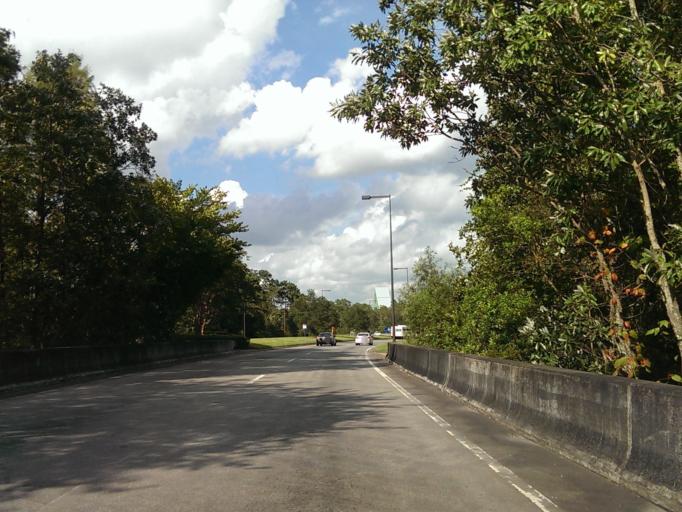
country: US
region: Florida
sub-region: Osceola County
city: Celebration
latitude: 28.3626
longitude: -81.5692
